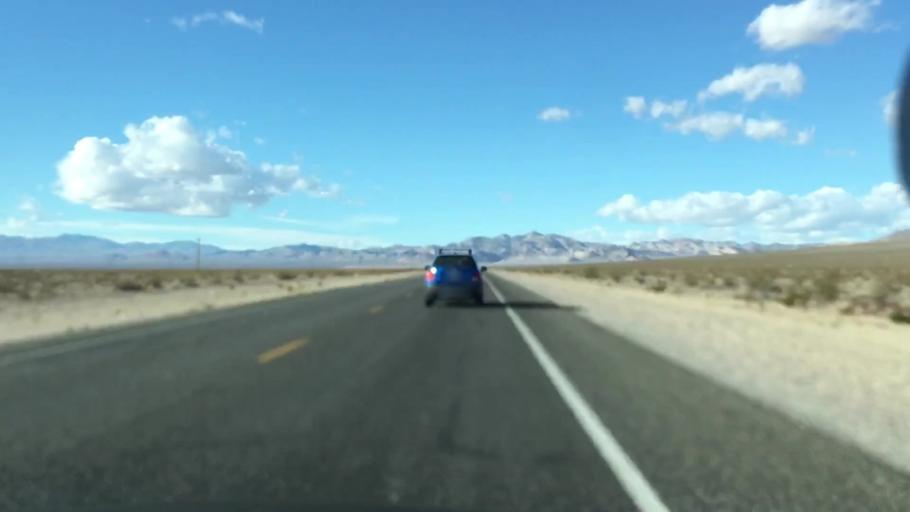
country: US
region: Nevada
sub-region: Nye County
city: Beatty
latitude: 36.7986
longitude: -116.7142
